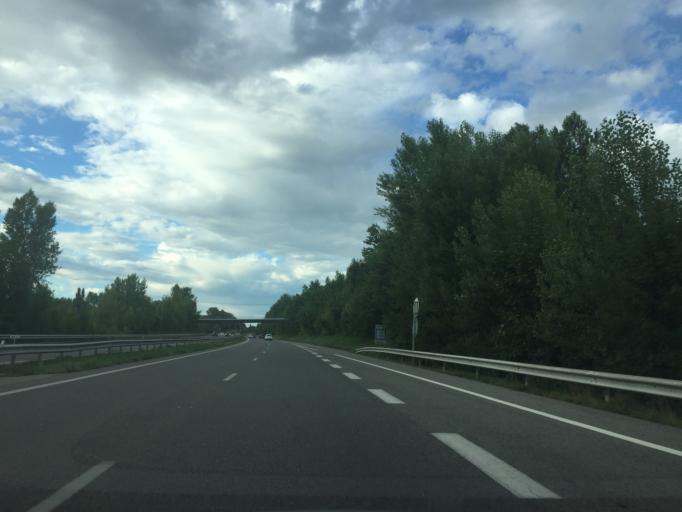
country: FR
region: Rhone-Alpes
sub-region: Departement de la Savoie
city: Mouxy
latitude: 45.6777
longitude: 5.9306
